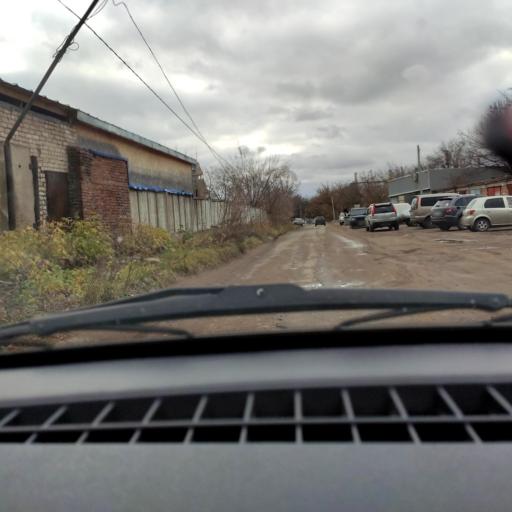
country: RU
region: Bashkortostan
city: Ufa
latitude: 54.8256
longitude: 56.0866
